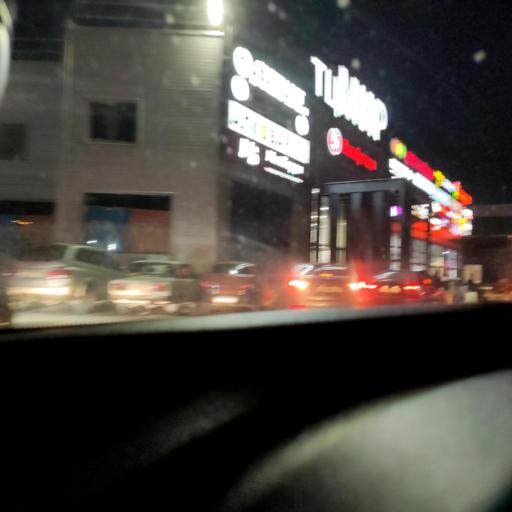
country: RU
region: Samara
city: Petra-Dubrava
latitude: 53.3160
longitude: 50.3038
